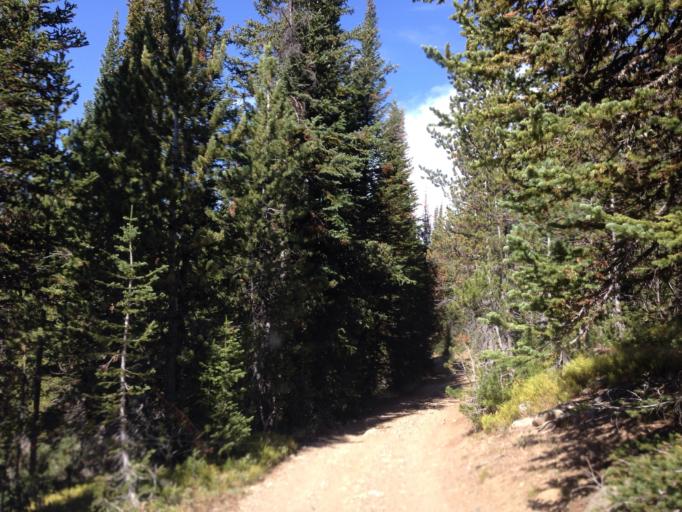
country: US
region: Montana
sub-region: Stillwater County
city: Absarokee
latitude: 45.0506
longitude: -109.9106
